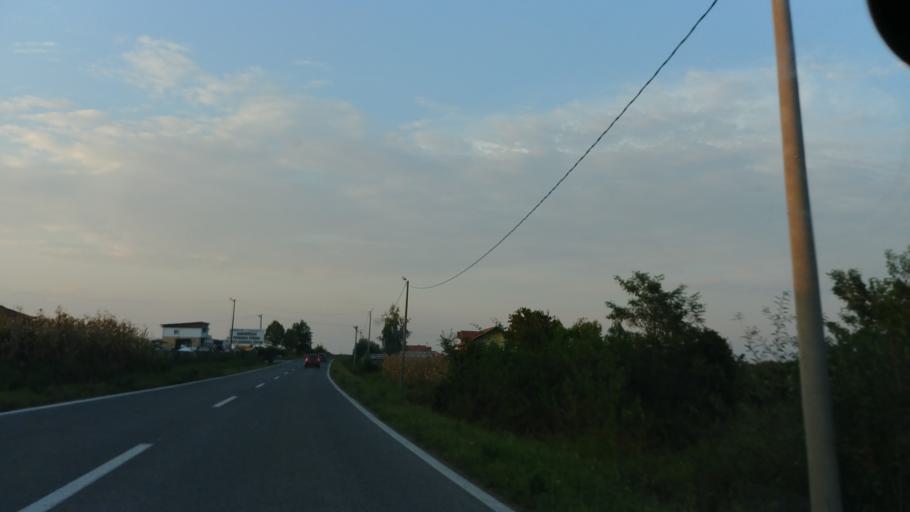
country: BA
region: Brcko
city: Brcko
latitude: 44.7749
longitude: 18.8096
